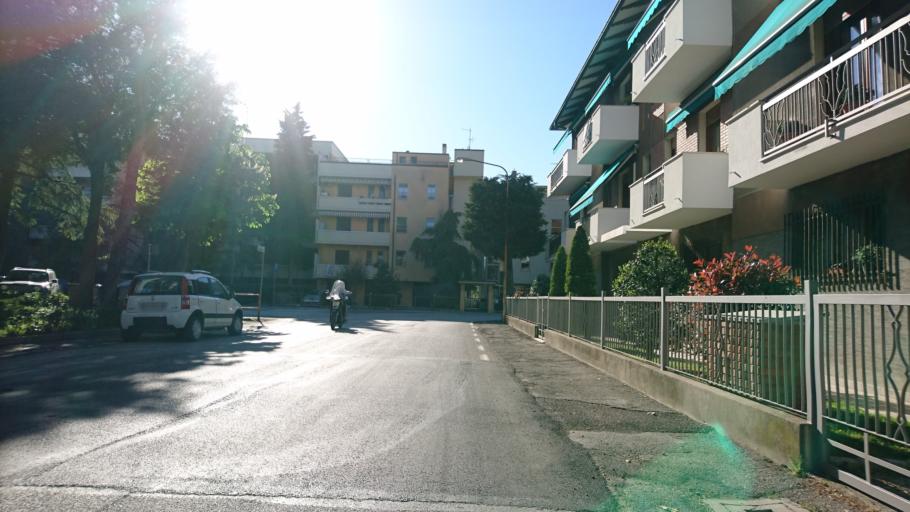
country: IT
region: The Marches
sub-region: Provincia di Pesaro e Urbino
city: Pesaro
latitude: 43.8940
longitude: 12.9065
